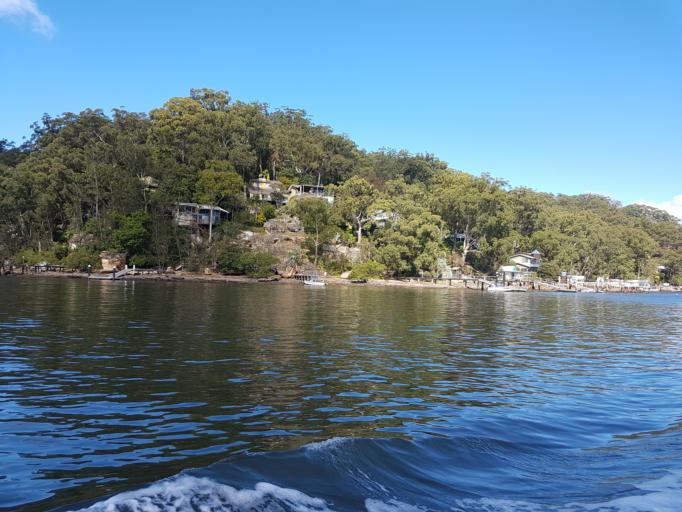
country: AU
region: New South Wales
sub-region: Gosford Shire
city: Umina
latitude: -33.5362
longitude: 151.2358
